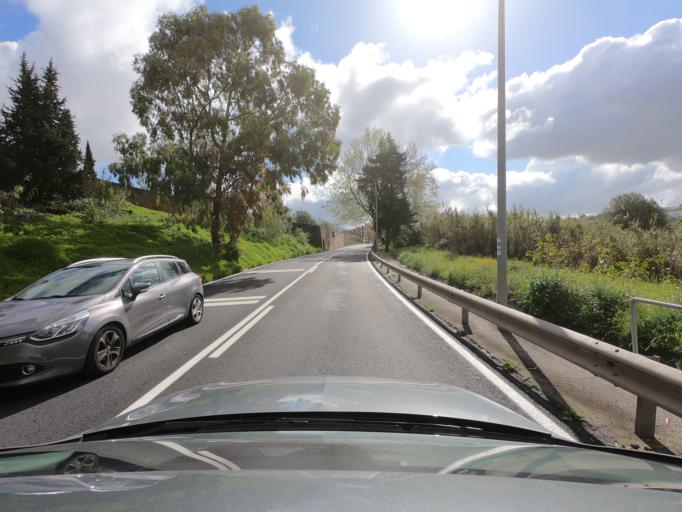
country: PT
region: Lisbon
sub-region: Oeiras
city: Carnaxide
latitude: 38.7251
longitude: -9.2528
